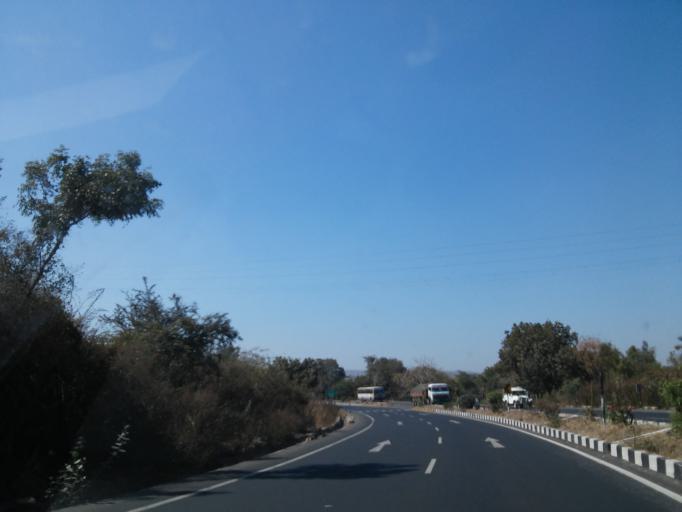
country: IN
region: Gujarat
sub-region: Sabar Kantha
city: Meghraj
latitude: 23.7421
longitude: 73.4273
